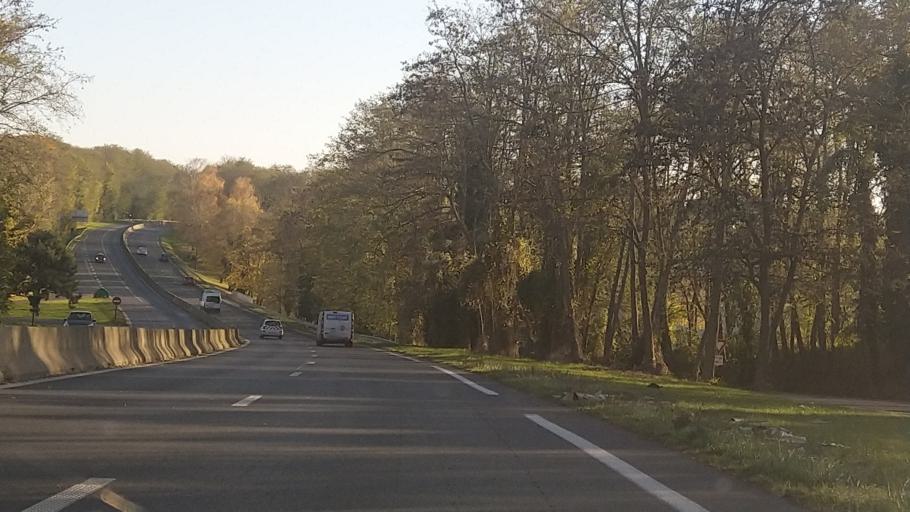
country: FR
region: Ile-de-France
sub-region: Departement du Val-d'Oise
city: Saint-Brice-sous-Foret
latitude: 49.0077
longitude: 2.3536
